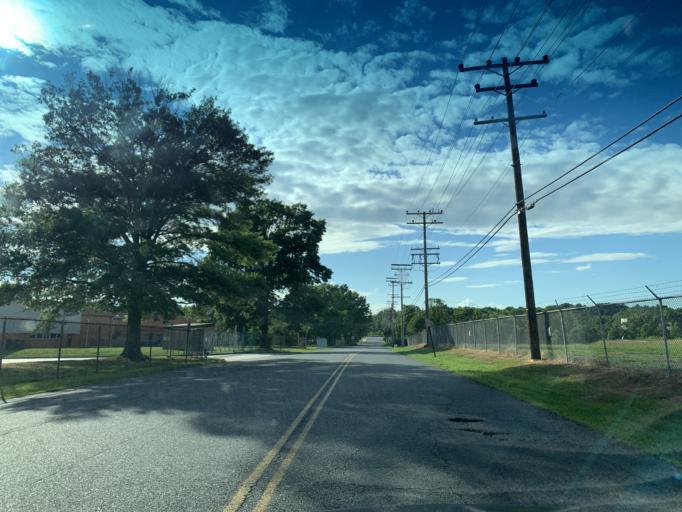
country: US
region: Maryland
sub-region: Harford County
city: Havre de Grace
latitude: 39.5346
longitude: -76.1090
